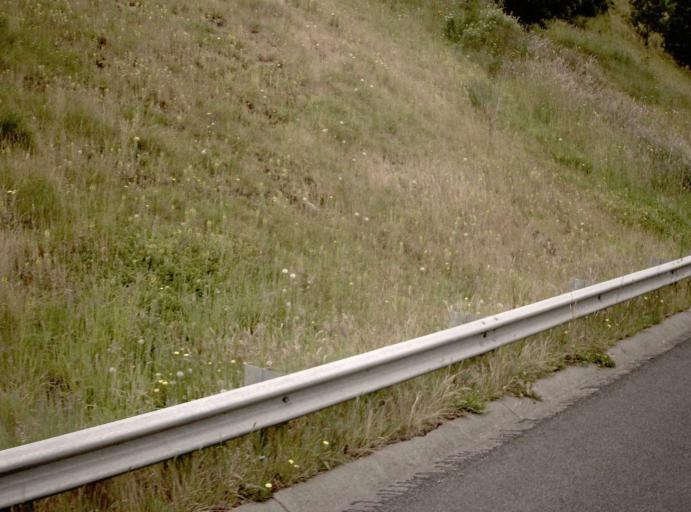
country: AU
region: Victoria
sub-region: Bass Coast
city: North Wonthaggi
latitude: -38.3773
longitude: 145.7282
